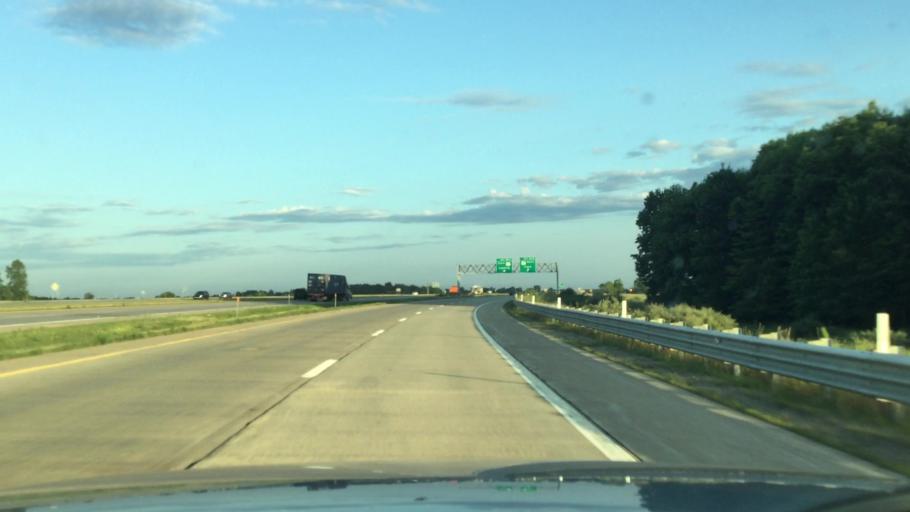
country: US
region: Michigan
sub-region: Clinton County
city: Bath
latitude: 42.8033
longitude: -84.5022
